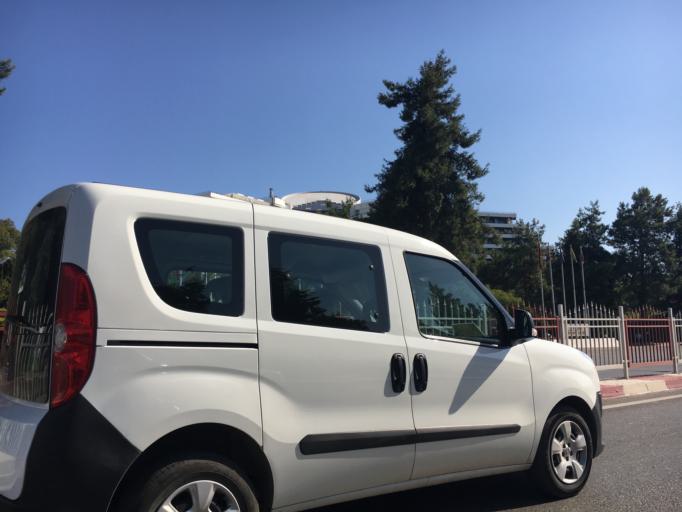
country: TR
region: Antalya
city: Antalya
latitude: 36.8874
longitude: 30.6752
